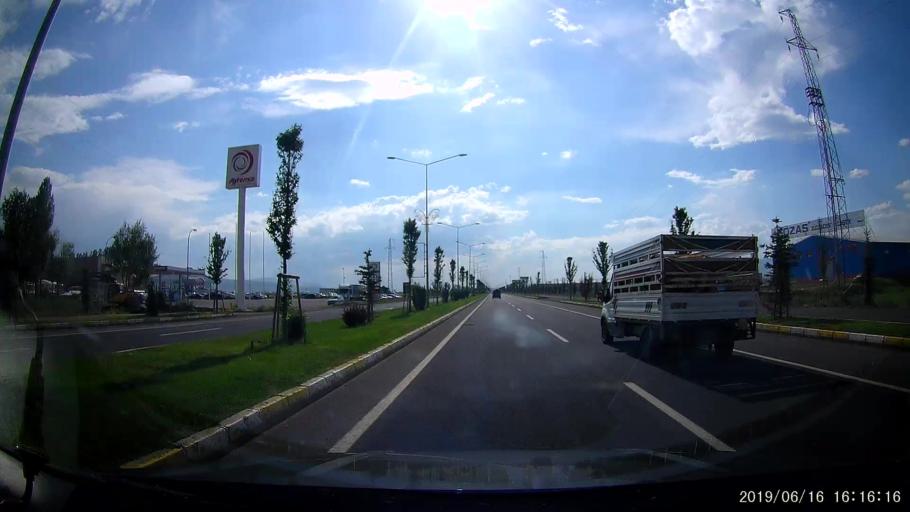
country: TR
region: Erzurum
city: Erzurum
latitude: 39.9628
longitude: 41.2091
